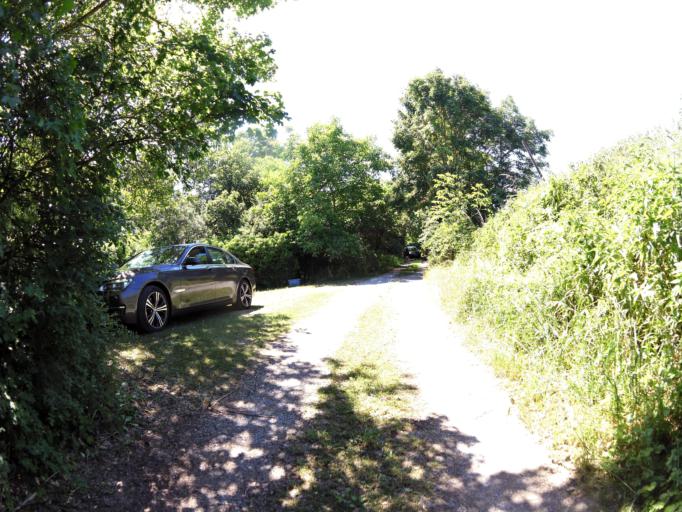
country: DE
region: Bavaria
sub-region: Regierungsbezirk Unterfranken
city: Ochsenfurt
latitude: 49.6722
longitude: 10.0702
